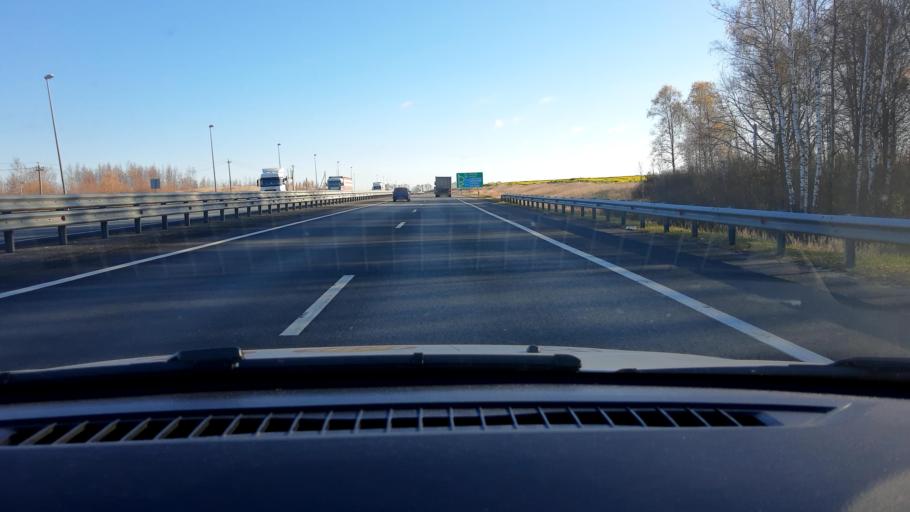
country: RU
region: Nizjnij Novgorod
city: Burevestnik
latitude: 56.1143
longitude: 43.8923
